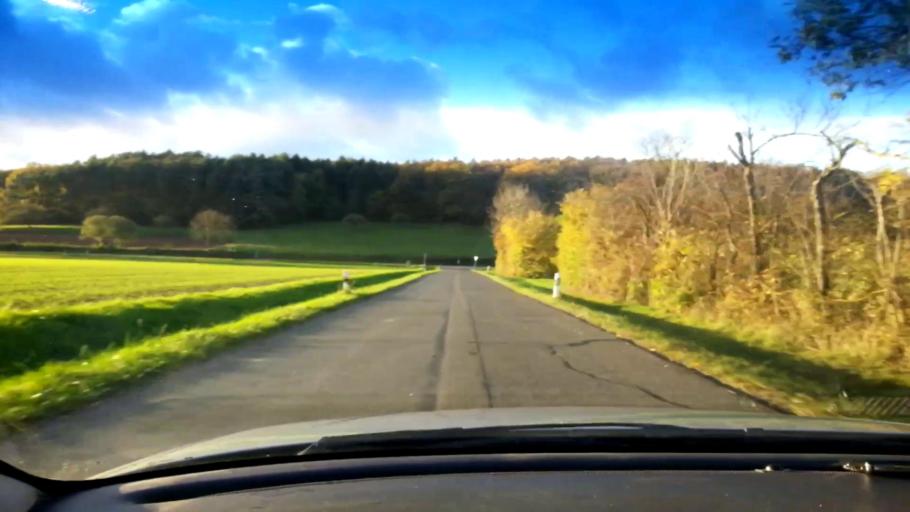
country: DE
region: Bavaria
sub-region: Upper Franconia
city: Zapfendorf
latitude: 50.0407
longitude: 10.9243
